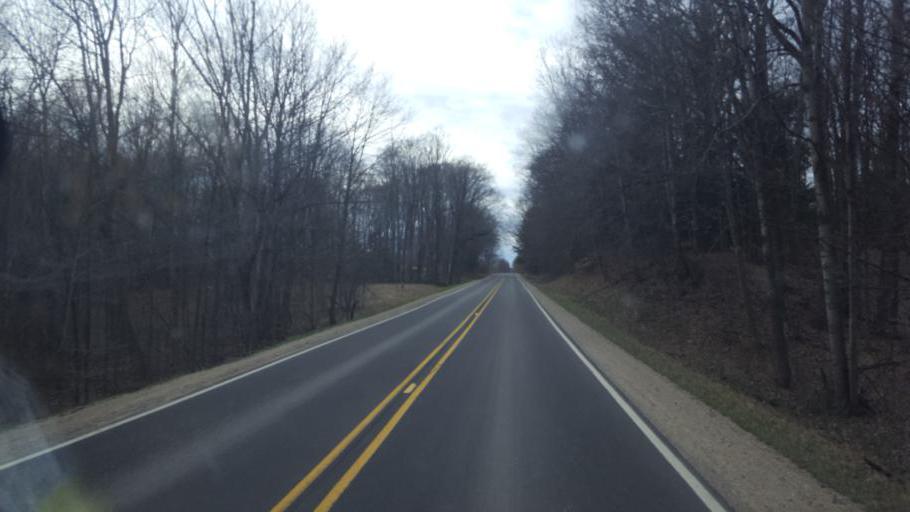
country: US
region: Michigan
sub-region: Montcalm County
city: Edmore
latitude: 43.5239
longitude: -85.0194
